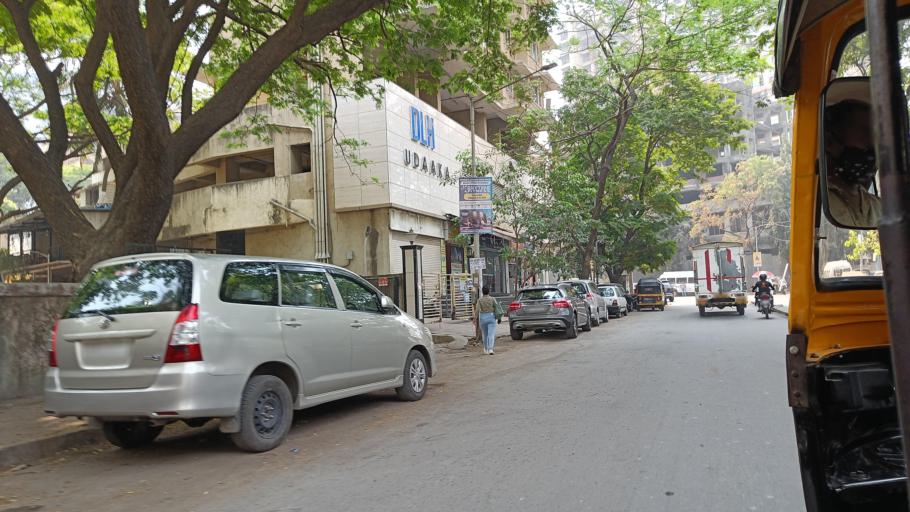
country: IN
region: Maharashtra
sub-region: Mumbai Suburban
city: Powai
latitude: 19.1531
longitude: 72.8436
